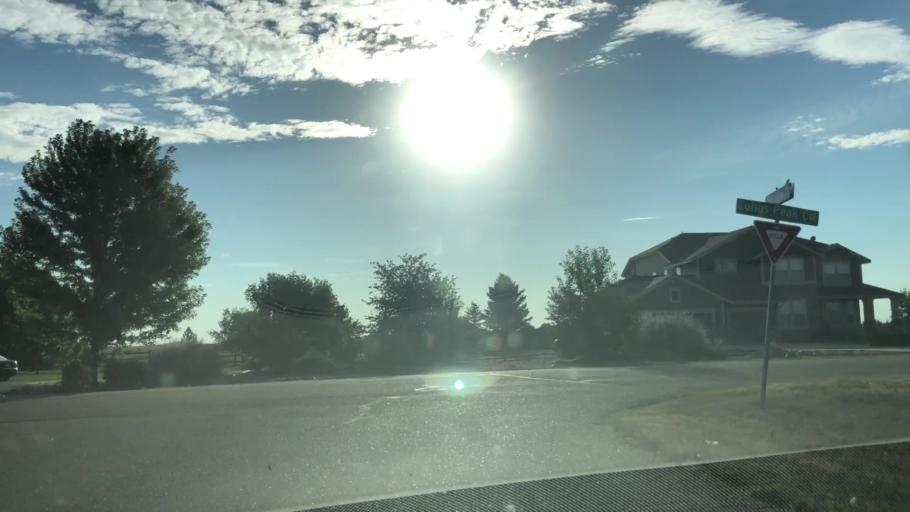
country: US
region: Colorado
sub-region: Weld County
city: Windsor
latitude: 40.4413
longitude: -104.9466
